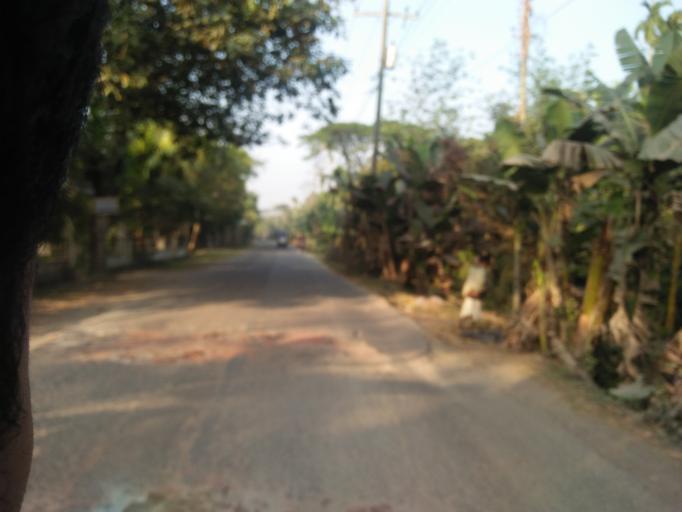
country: BD
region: Barisal
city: Bhola
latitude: 22.7422
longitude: 90.6343
